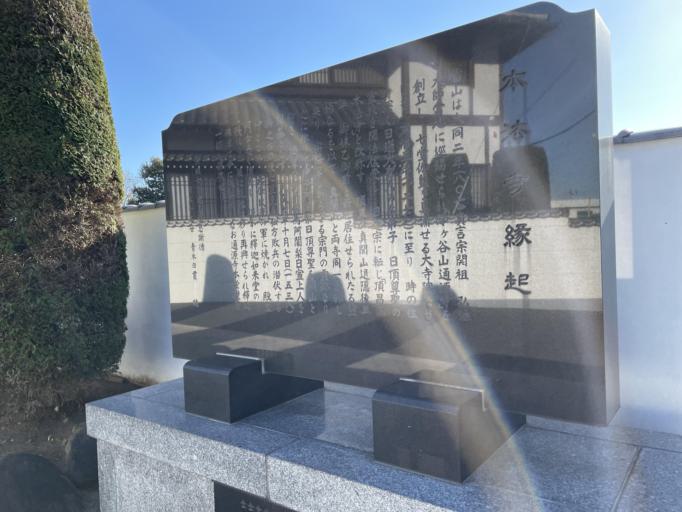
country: JP
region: Chiba
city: Matsudo
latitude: 35.7750
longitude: 139.9277
